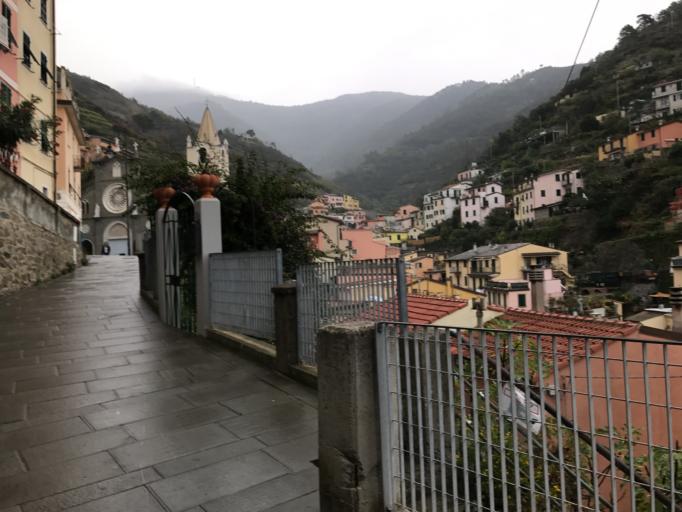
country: IT
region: Liguria
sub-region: Provincia di La Spezia
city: Riomaggiore
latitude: 44.1002
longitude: 9.7387
